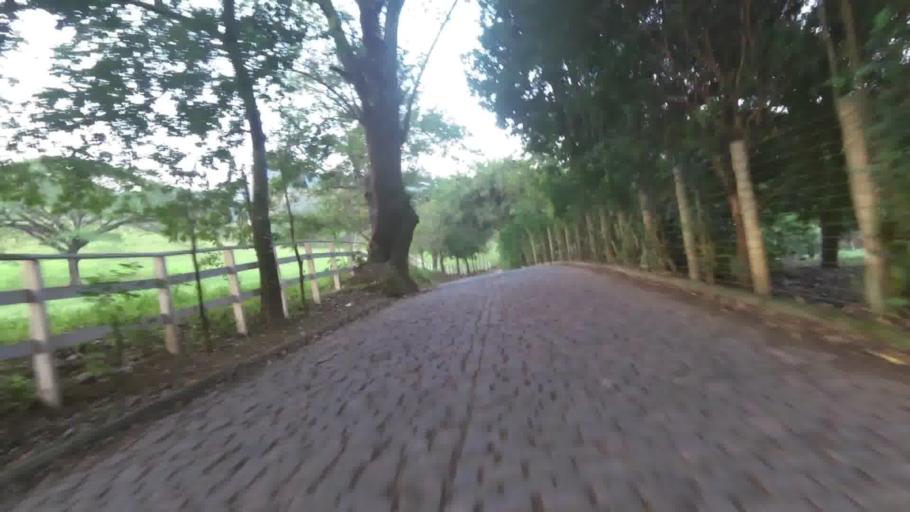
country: BR
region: Espirito Santo
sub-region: Alfredo Chaves
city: Alfredo Chaves
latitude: -20.6500
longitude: -40.6438
